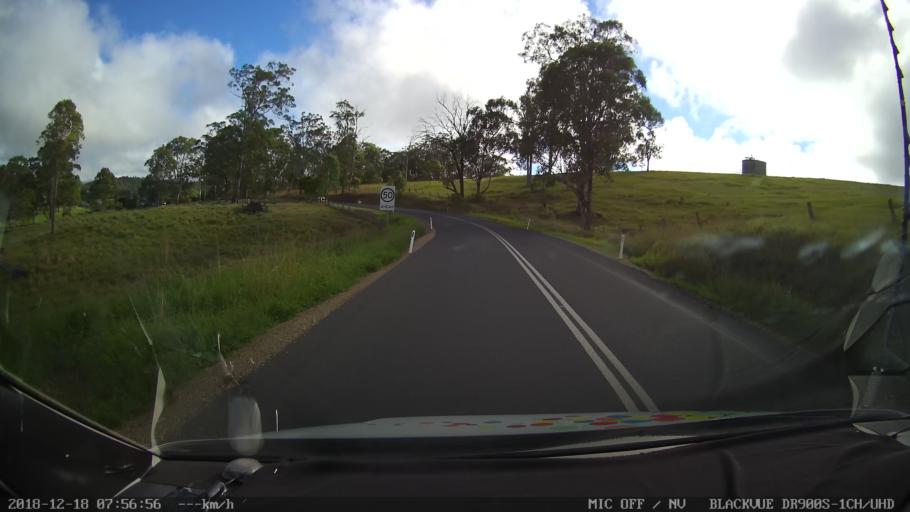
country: AU
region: New South Wales
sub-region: Kyogle
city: Kyogle
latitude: -28.3965
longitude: 152.6098
